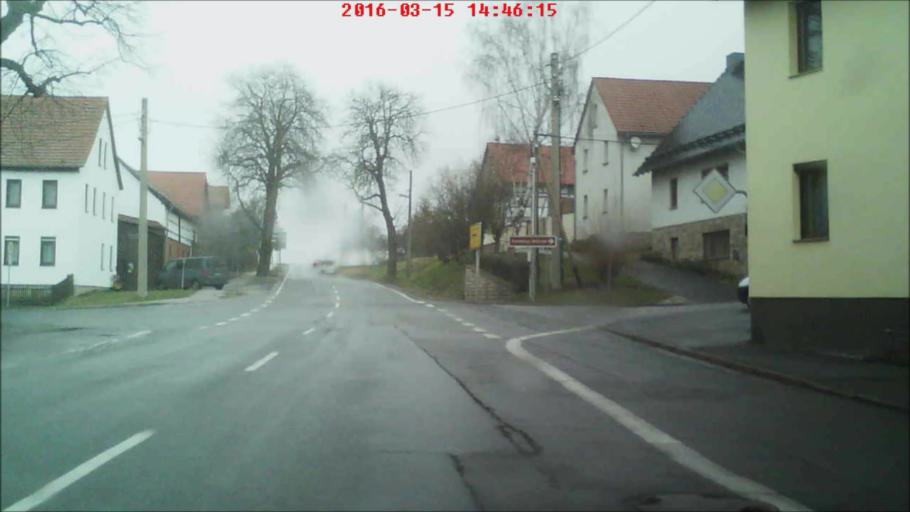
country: DE
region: Thuringia
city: Rockhausen
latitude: 50.9169
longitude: 11.0517
